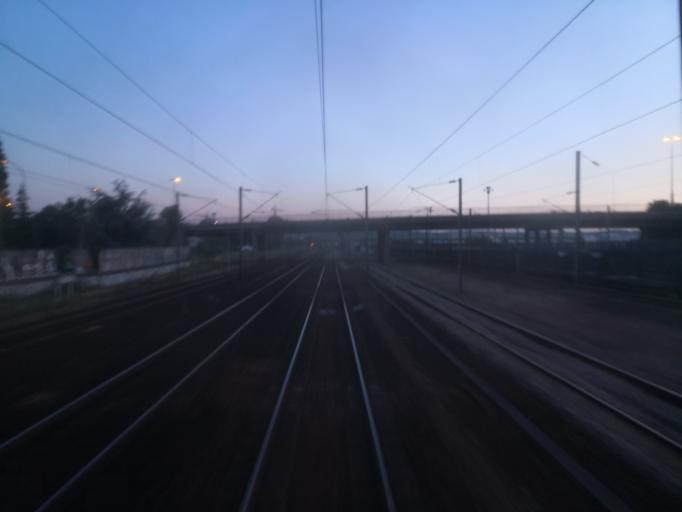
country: FR
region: Ile-de-France
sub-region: Departement des Yvelines
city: Poissy
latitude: 48.9396
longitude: 2.0554
